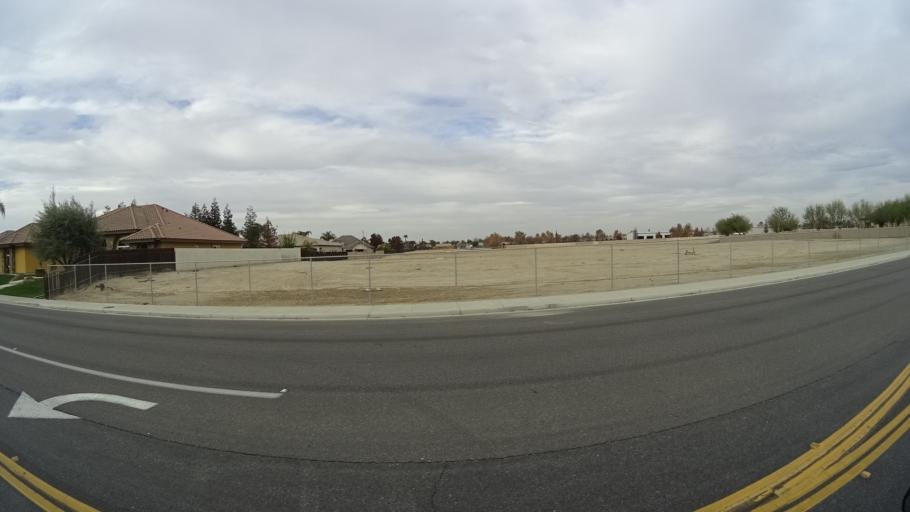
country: US
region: California
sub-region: Kern County
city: Rosedale
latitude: 35.4123
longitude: -119.1407
